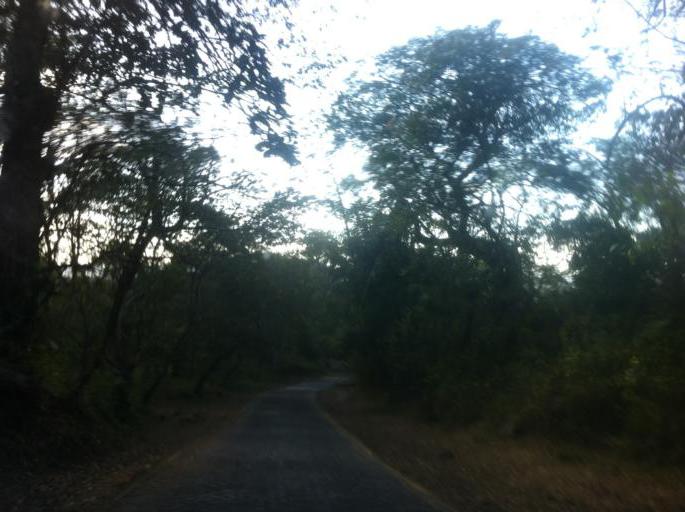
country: NI
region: Granada
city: Diriomo
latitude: 11.8415
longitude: -86.0006
